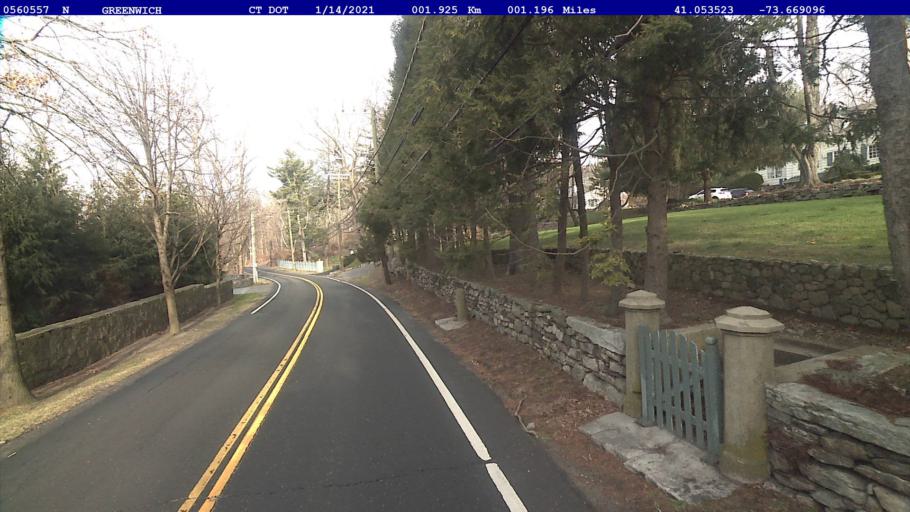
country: US
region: Connecticut
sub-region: Fairfield County
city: Glenville
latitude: 41.0535
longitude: -73.6691
